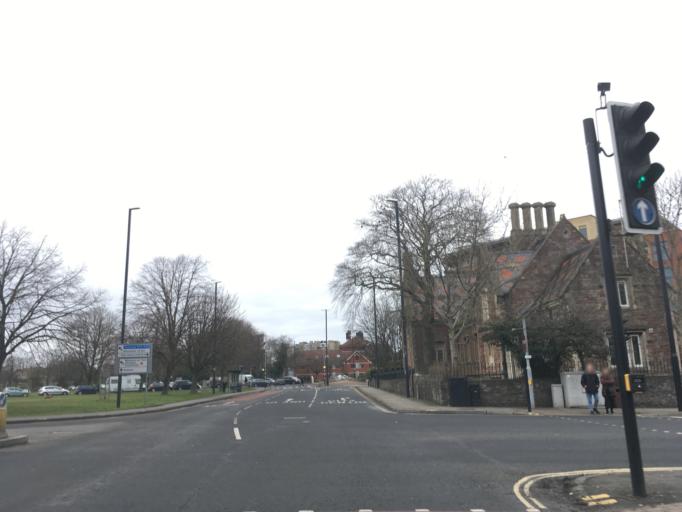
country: GB
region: England
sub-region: Bristol
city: Bristol
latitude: 51.4707
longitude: -2.6165
